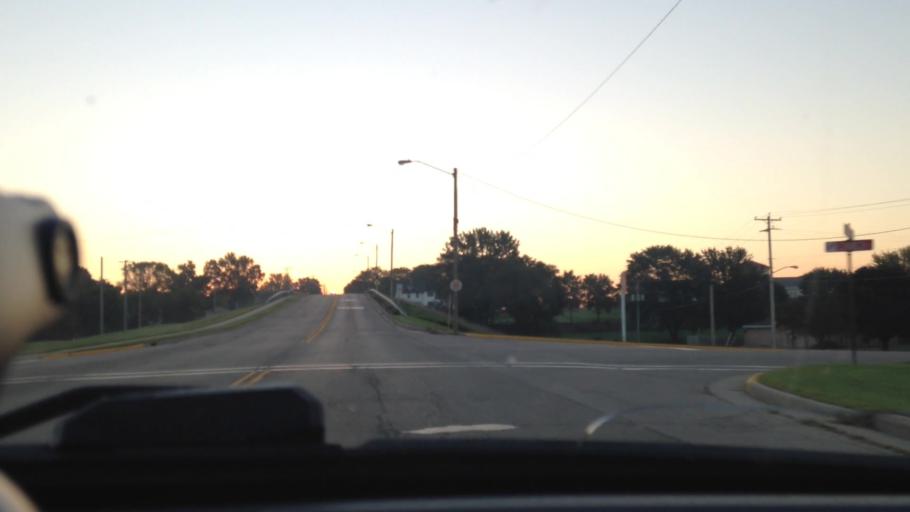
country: US
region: Wisconsin
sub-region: Dodge County
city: Lomira
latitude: 43.5871
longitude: -88.4443
